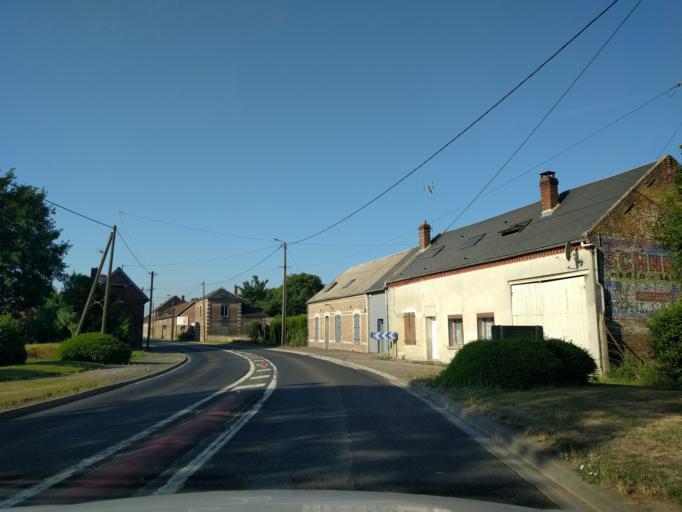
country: FR
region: Picardie
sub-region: Departement de la Somme
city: Chaulnes
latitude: 49.8368
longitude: 2.8657
